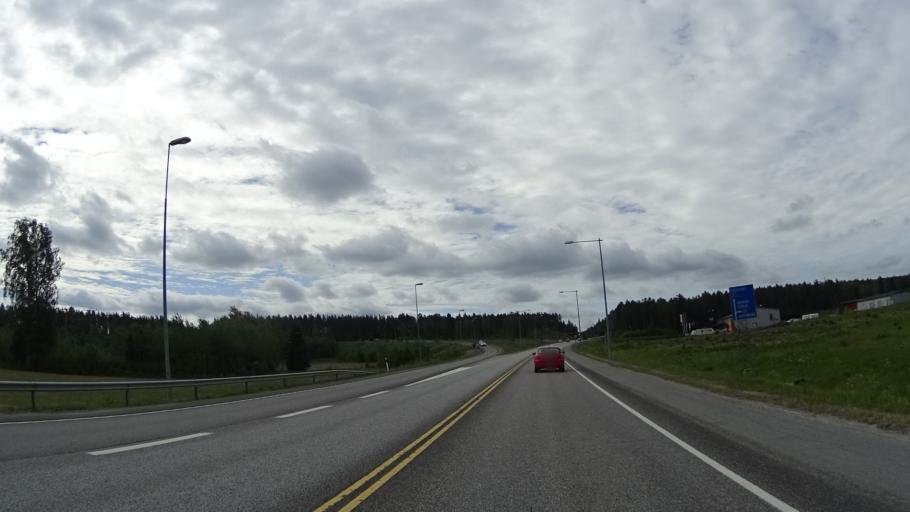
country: FI
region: Uusimaa
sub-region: Helsinki
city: Vihti
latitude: 60.3563
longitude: 24.3274
